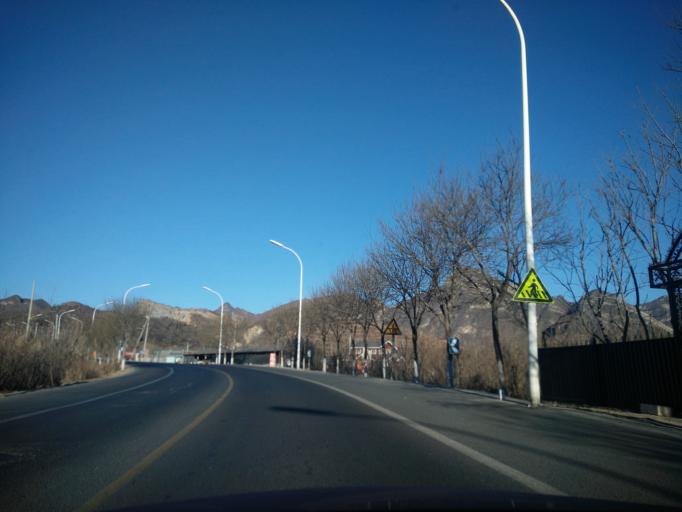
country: CN
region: Beijing
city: Junzhuang
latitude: 39.9908
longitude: 116.0797
